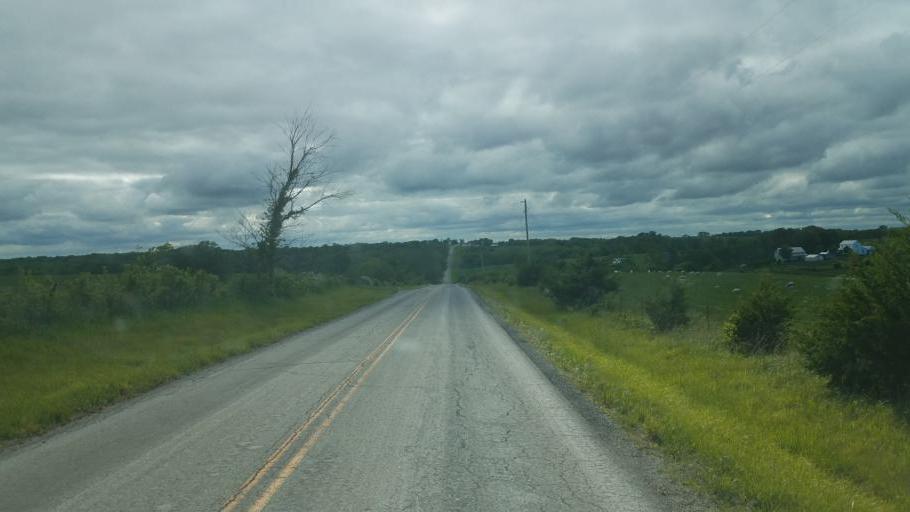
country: US
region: Missouri
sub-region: Mercer County
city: Princeton
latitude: 40.2493
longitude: -93.6807
